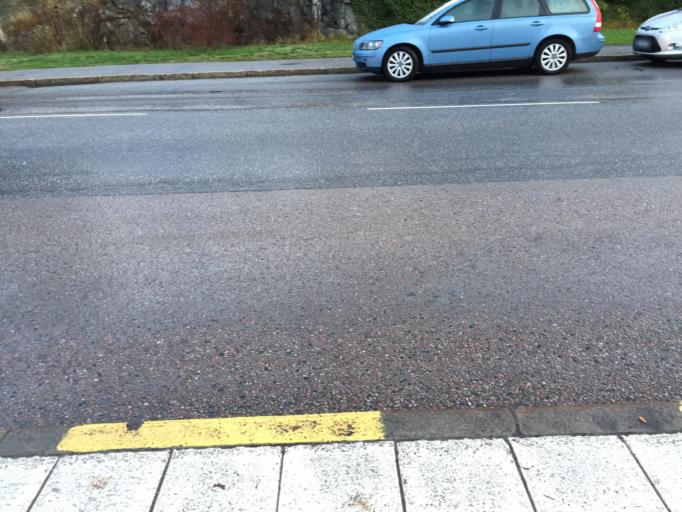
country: SE
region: Stockholm
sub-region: Stockholms Kommun
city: Arsta
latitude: 59.2983
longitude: 18.0613
